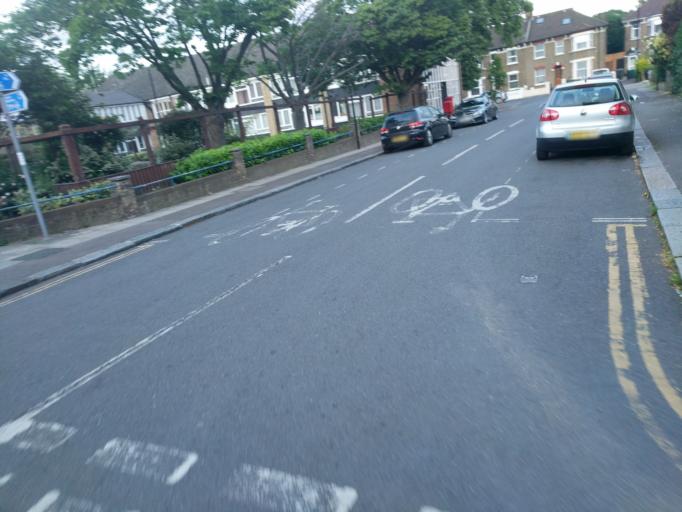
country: GB
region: England
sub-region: Greater London
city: Catford
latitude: 51.4582
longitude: -0.0193
